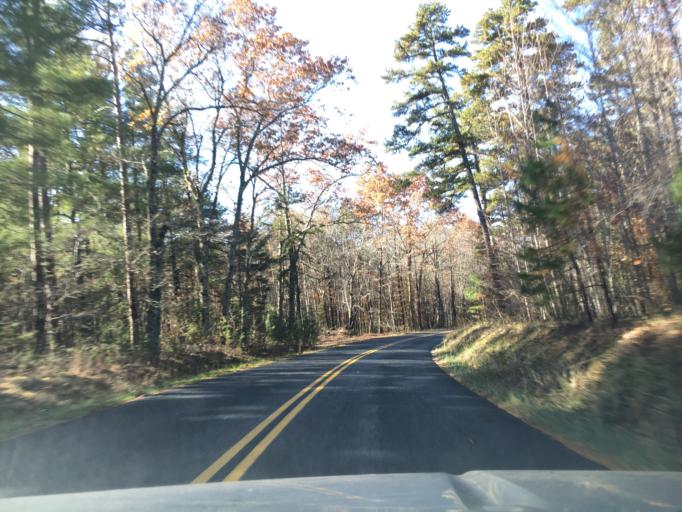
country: US
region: Virginia
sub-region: Buckingham County
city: Buckingham
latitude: 37.4338
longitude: -78.6487
